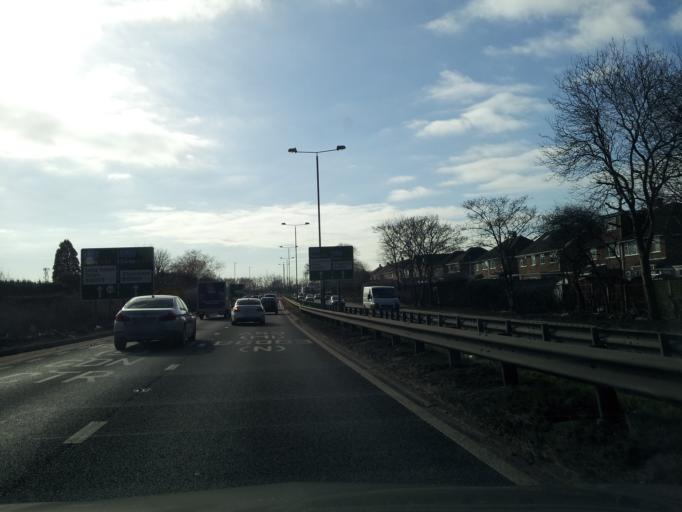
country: GB
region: England
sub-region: Derbyshire
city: Long Eaton
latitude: 52.9223
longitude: -1.2627
